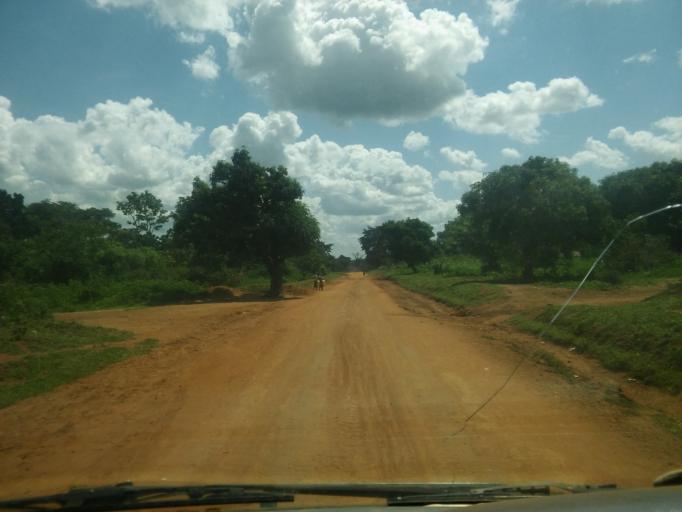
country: UG
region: Eastern Region
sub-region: Pallisa District
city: Pallisa
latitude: 1.1542
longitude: 33.8004
